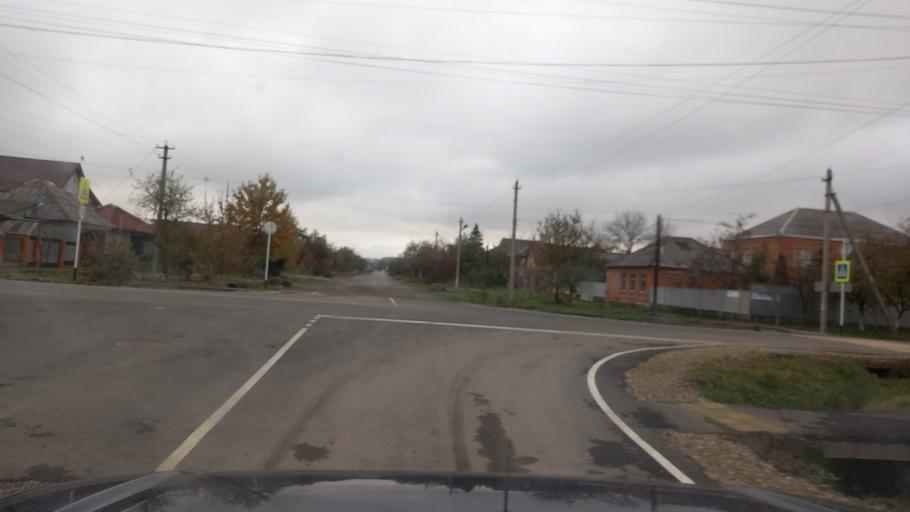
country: RU
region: Adygeya
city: Maykop
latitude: 44.6191
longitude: 40.1262
